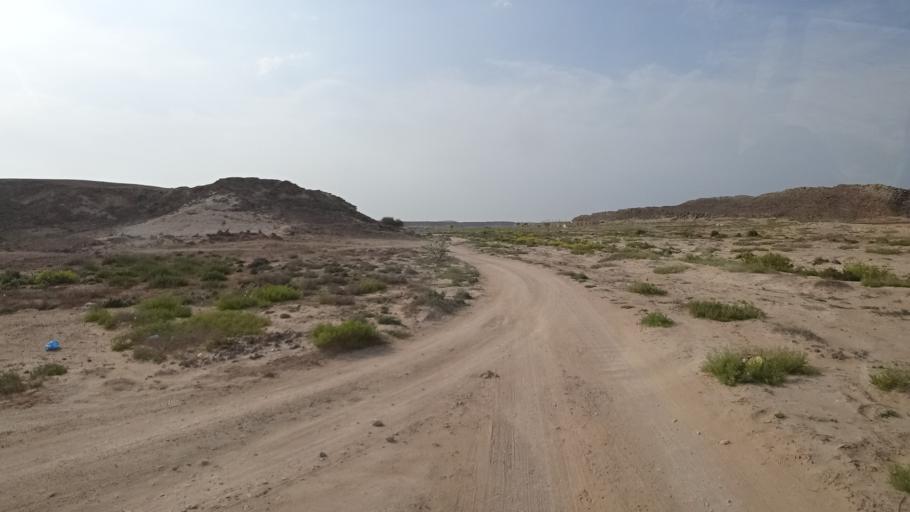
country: OM
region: Ash Sharqiyah
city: Sur
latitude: 22.4304
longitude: 59.8320
